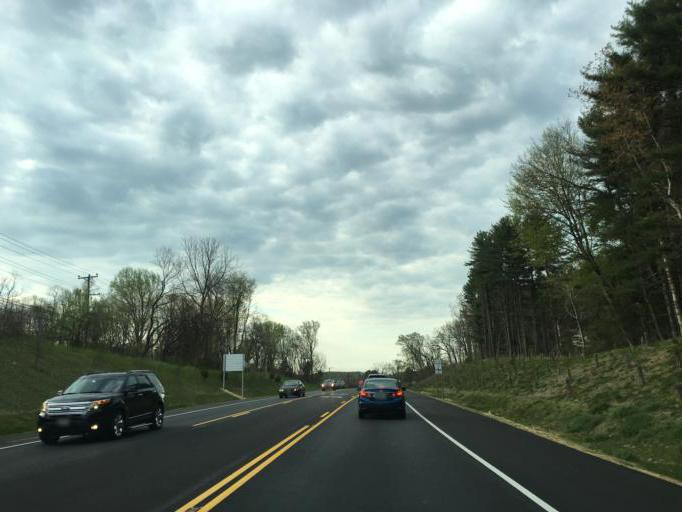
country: US
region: Maryland
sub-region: Carroll County
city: Sykesville
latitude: 39.3551
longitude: -76.9675
